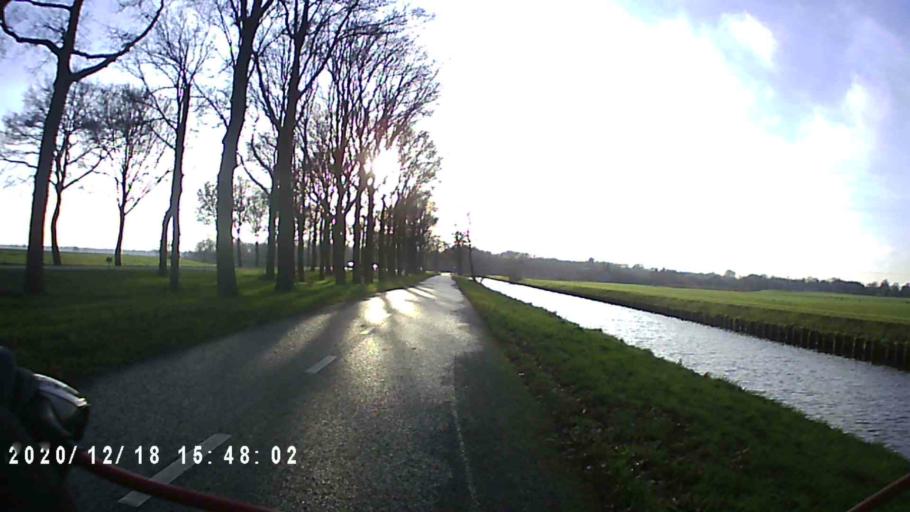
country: NL
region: Drenthe
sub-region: Gemeente Tynaarlo
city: Zuidlaren
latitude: 53.1026
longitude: 6.7013
